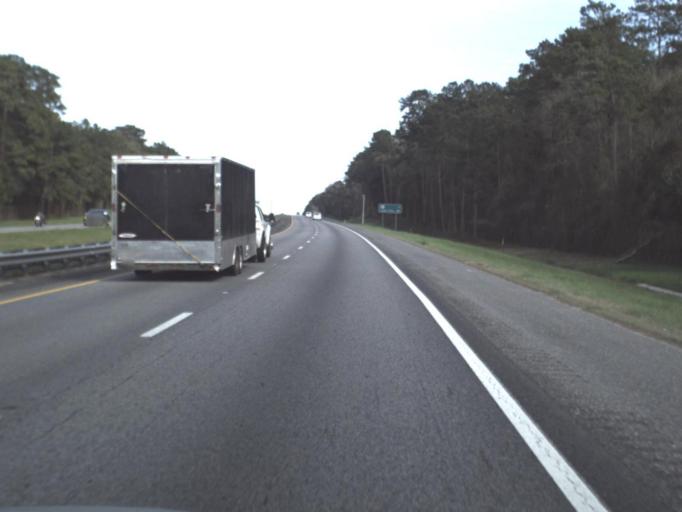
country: US
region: Florida
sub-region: Leon County
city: Tallahassee
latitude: 30.4782
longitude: -84.1417
